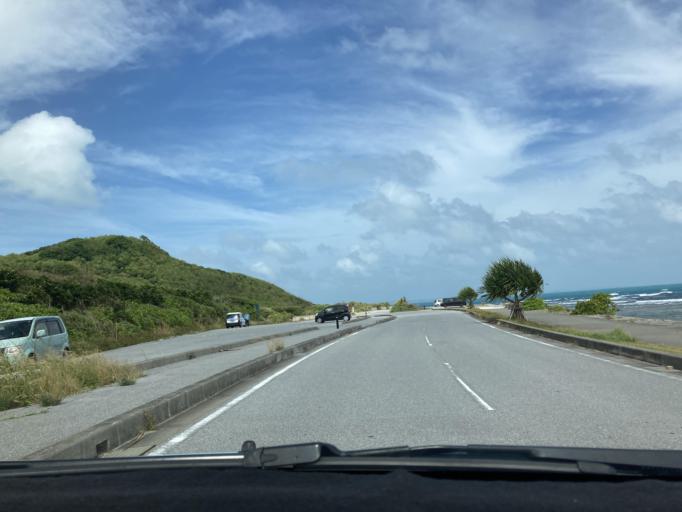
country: JP
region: Okinawa
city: Ginowan
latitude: 26.1858
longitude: 127.8217
